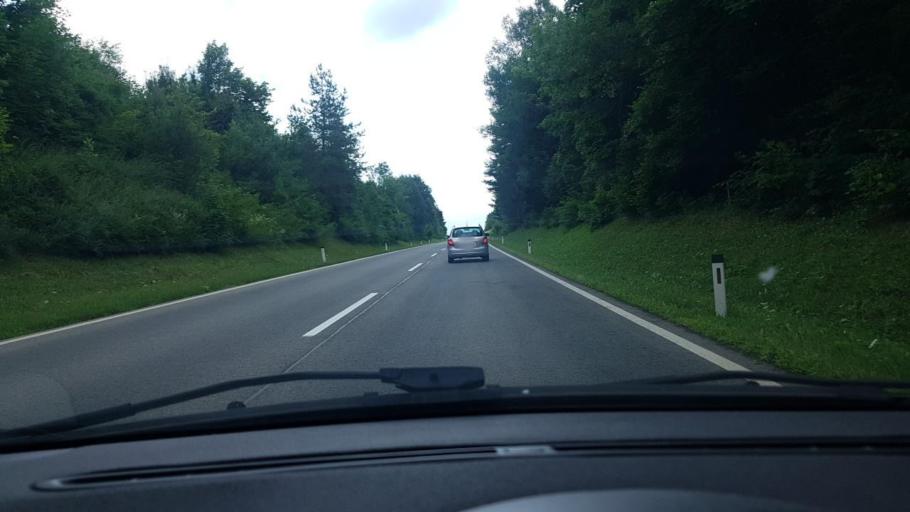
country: AT
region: Carinthia
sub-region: Politischer Bezirk Villach Land
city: Stockenboi
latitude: 46.6210
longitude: 13.5044
